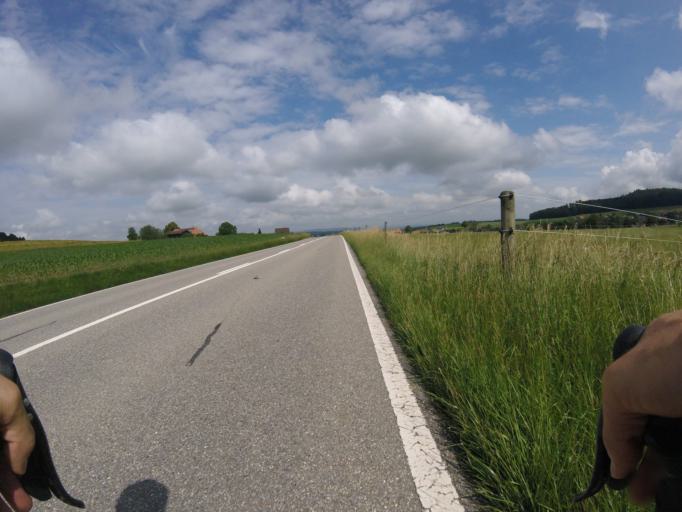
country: CH
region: Bern
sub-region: Emmental District
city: Hindelbank
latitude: 47.0270
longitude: 7.5524
